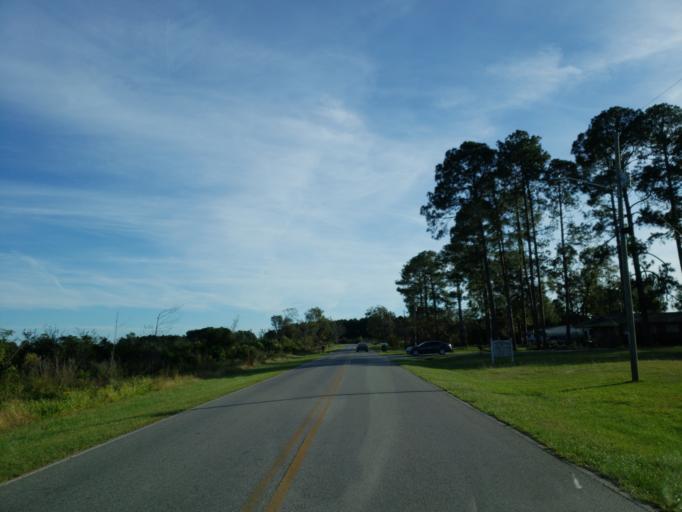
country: US
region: Georgia
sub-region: Dooly County
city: Vienna
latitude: 32.0814
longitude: -83.7879
